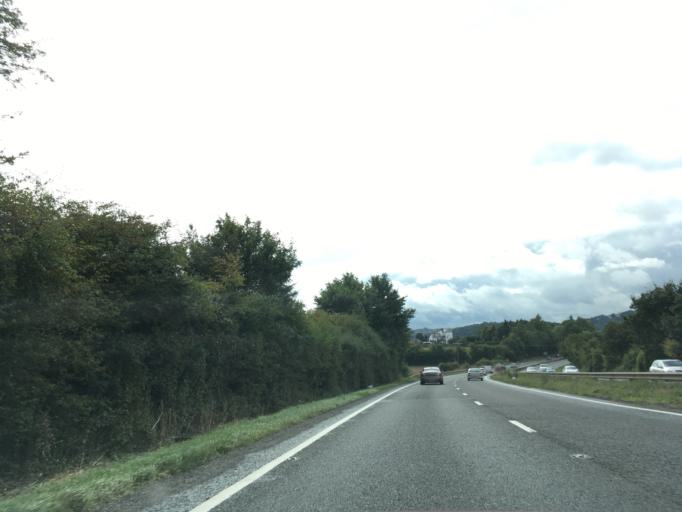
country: GB
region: England
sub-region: Herefordshire
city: Marstow
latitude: 51.8716
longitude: -2.6298
